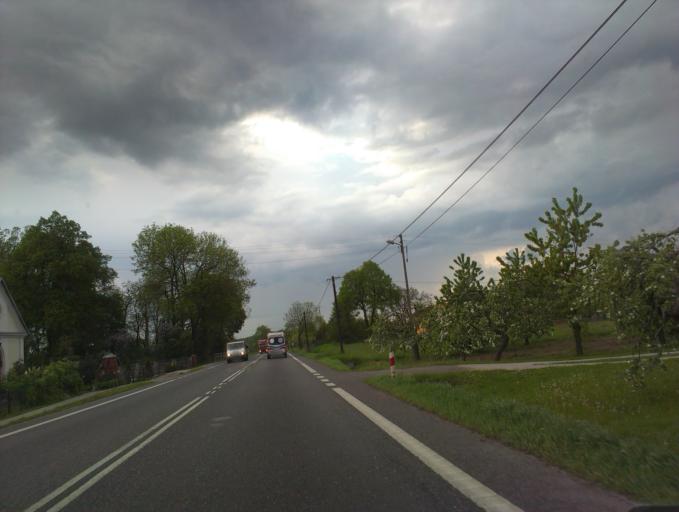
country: PL
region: Masovian Voivodeship
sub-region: Powiat grojecki
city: Pniewy
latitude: 51.9182
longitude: 20.6807
